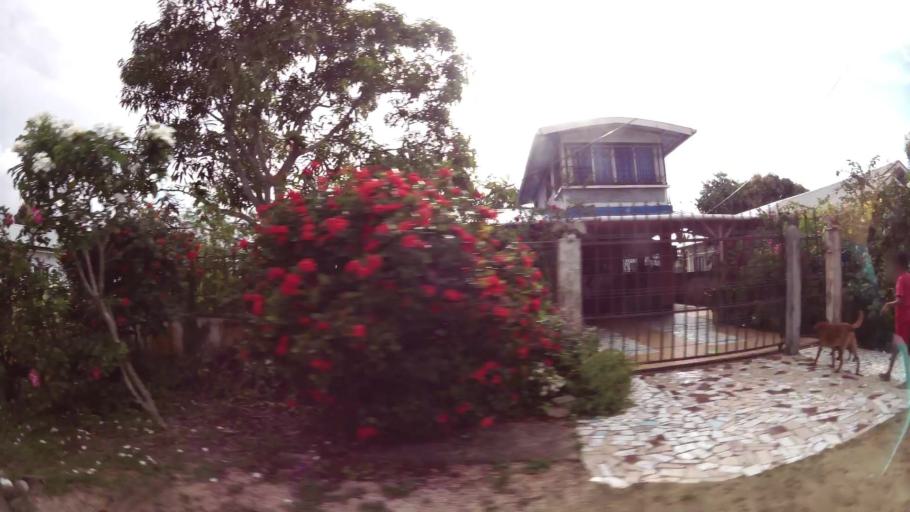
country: SR
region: Paramaribo
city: Paramaribo
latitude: 5.8486
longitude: -55.1781
